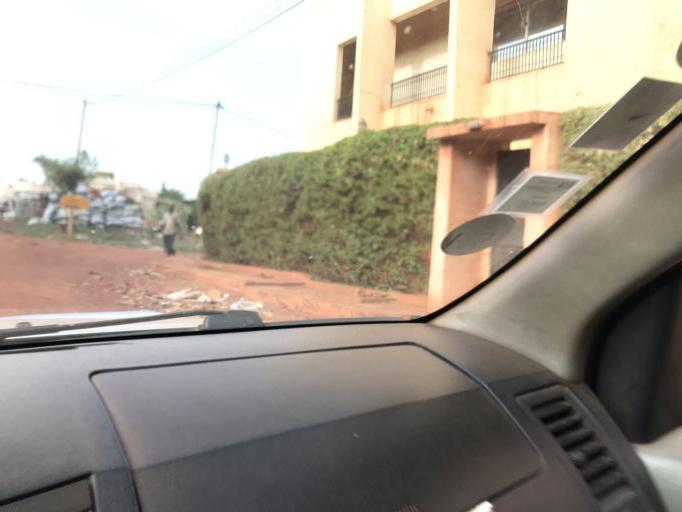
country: ML
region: Bamako
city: Bamako
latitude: 12.5830
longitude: -8.0078
